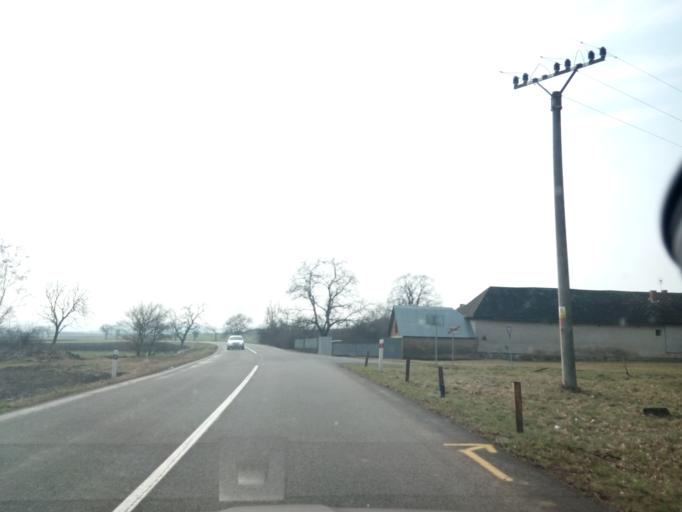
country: SK
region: Kosicky
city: Trebisov
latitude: 48.5779
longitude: 21.6406
